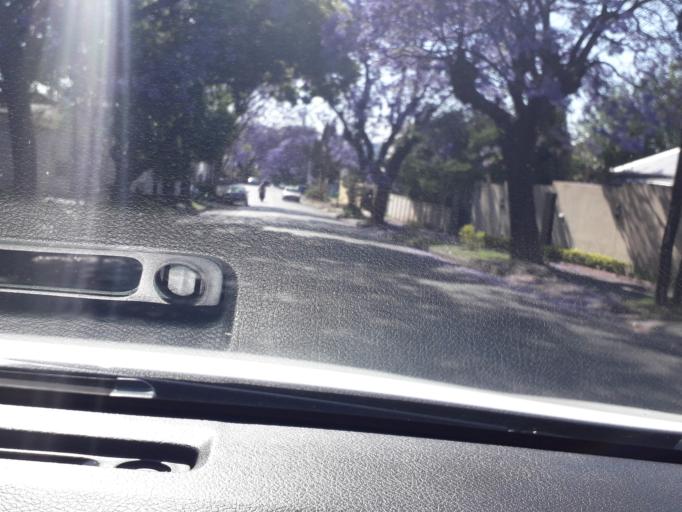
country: ZA
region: Gauteng
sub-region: City of Johannesburg Metropolitan Municipality
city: Johannesburg
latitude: -26.1776
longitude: 28.0073
